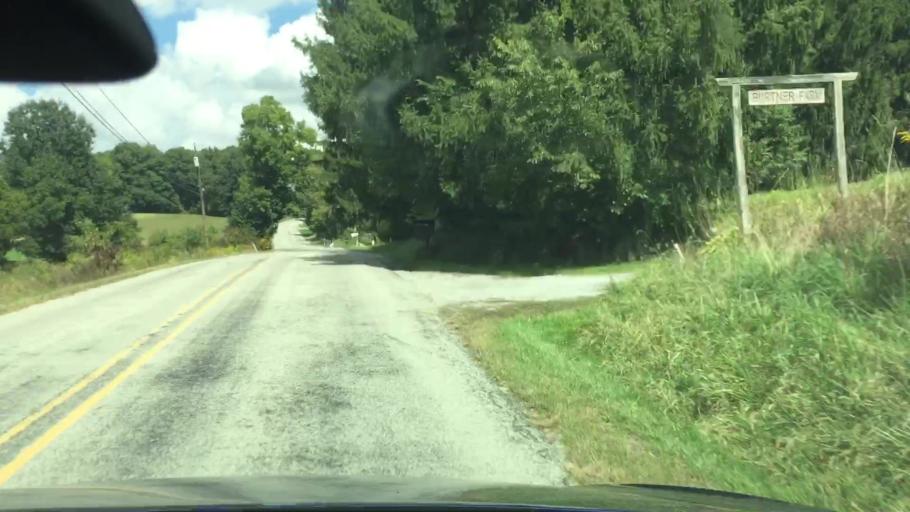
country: US
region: Pennsylvania
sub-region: Butler County
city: Oak Hills
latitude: 40.7906
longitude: -79.8714
